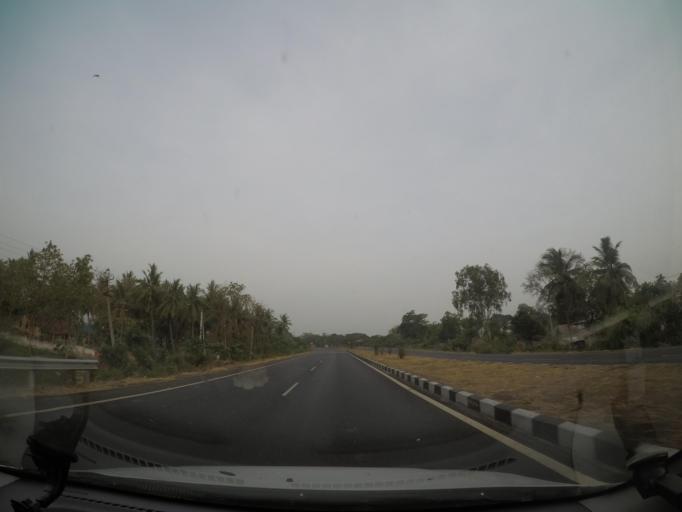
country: IN
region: Andhra Pradesh
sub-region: Krishna
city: Gannavaram
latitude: 16.6105
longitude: 80.9149
